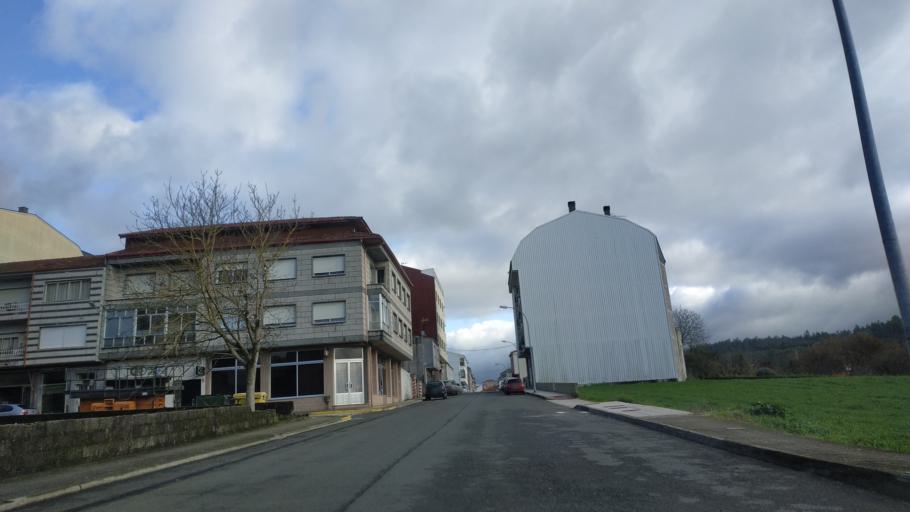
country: ES
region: Galicia
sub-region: Provincia de Pontevedra
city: Silleda
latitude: 42.7929
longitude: -8.1691
